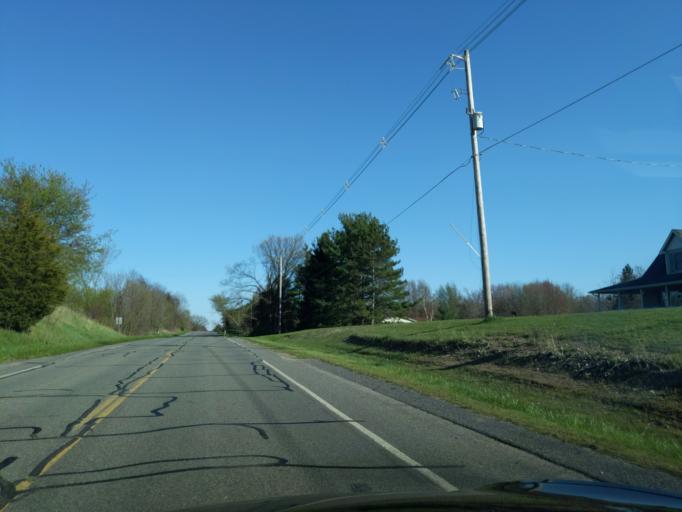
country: US
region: Michigan
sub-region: Ionia County
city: Portland
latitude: 42.8316
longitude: -84.8514
